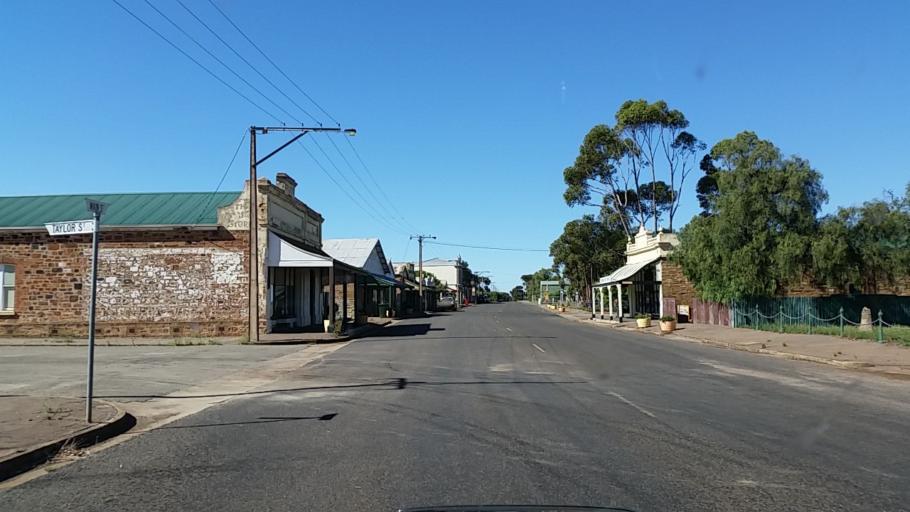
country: AU
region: South Australia
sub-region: Peterborough
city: Peterborough
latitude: -33.1507
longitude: 138.9190
